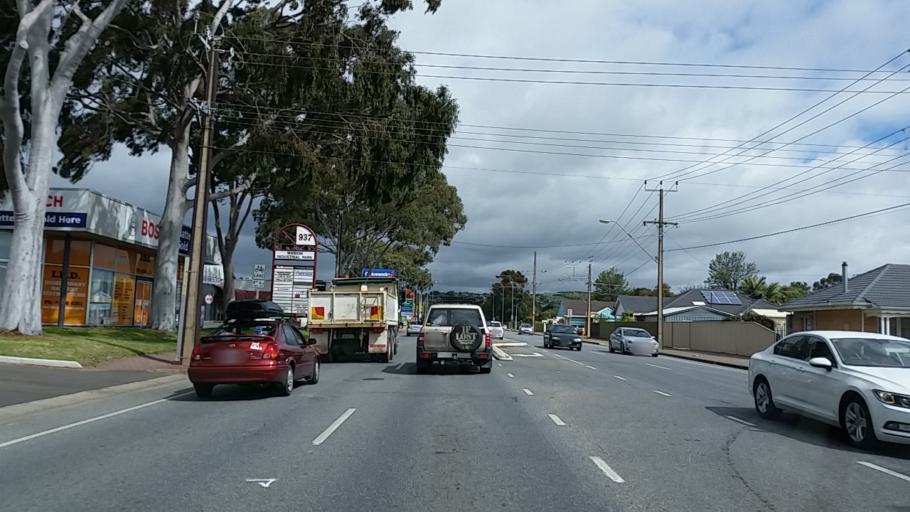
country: AU
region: South Australia
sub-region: Marion
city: Marion
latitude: -35.0132
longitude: 138.5585
